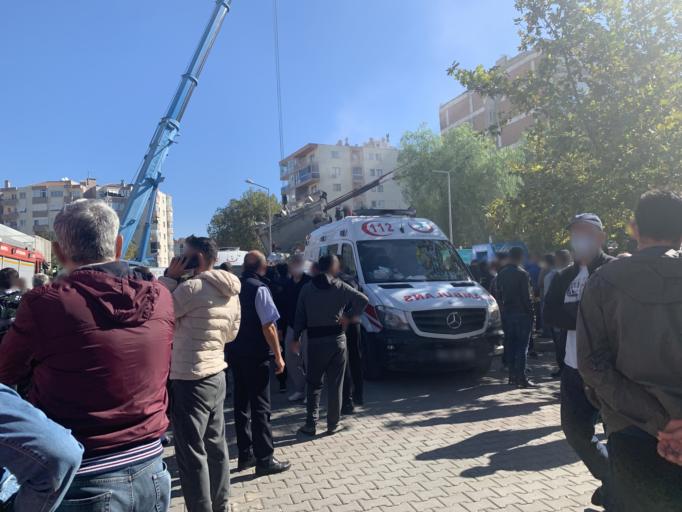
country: TR
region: Izmir
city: Bornova
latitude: 38.4587
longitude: 27.1947
